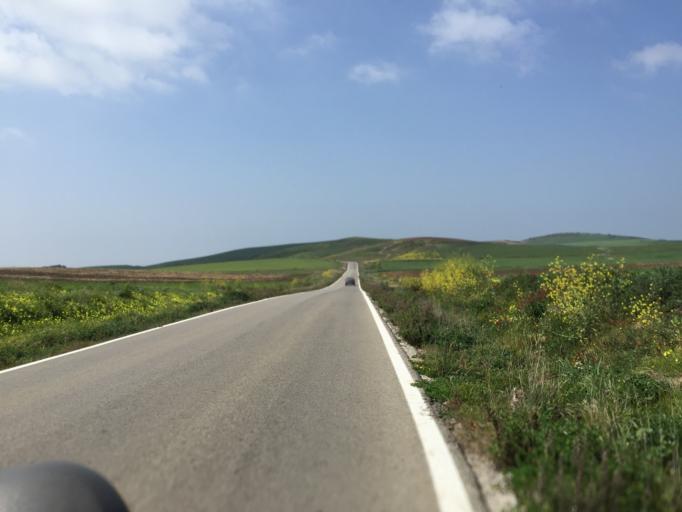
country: ES
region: Andalusia
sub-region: Provincia de Cadiz
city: Vejer de la Frontera
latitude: 36.2360
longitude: -6.0226
